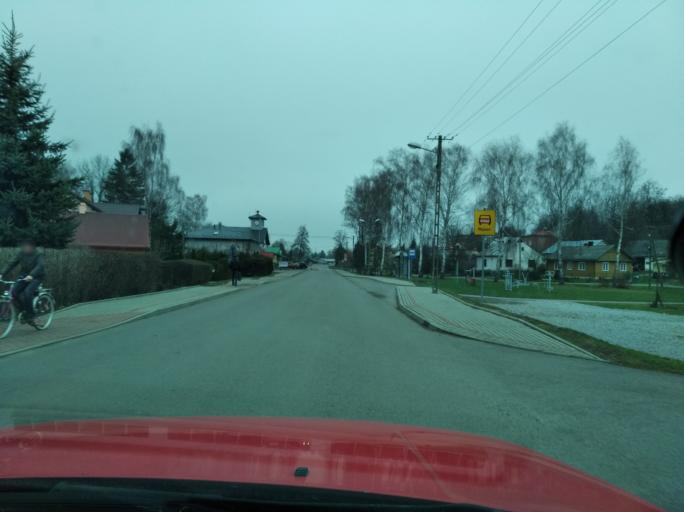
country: PL
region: Subcarpathian Voivodeship
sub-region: Powiat jaroslawski
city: Pawlosiow
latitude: 49.9965
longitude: 22.6473
